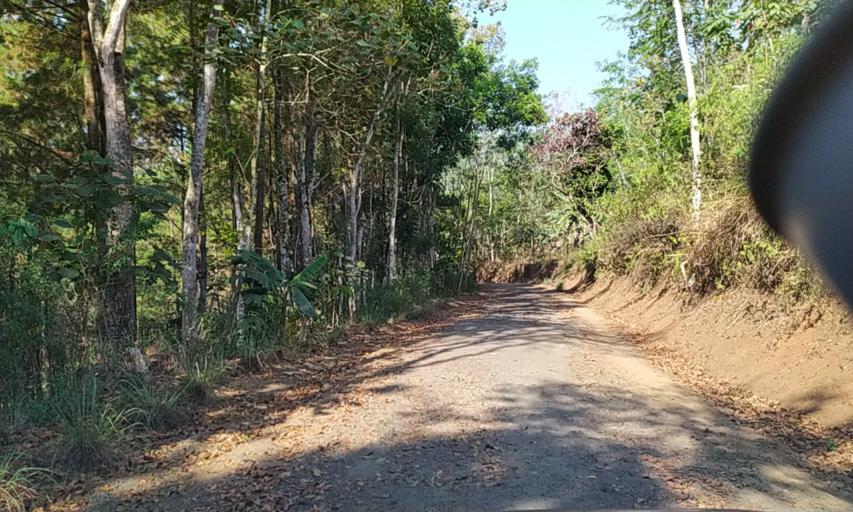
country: ID
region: Central Java
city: Datar
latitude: -7.2164
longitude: 108.6245
